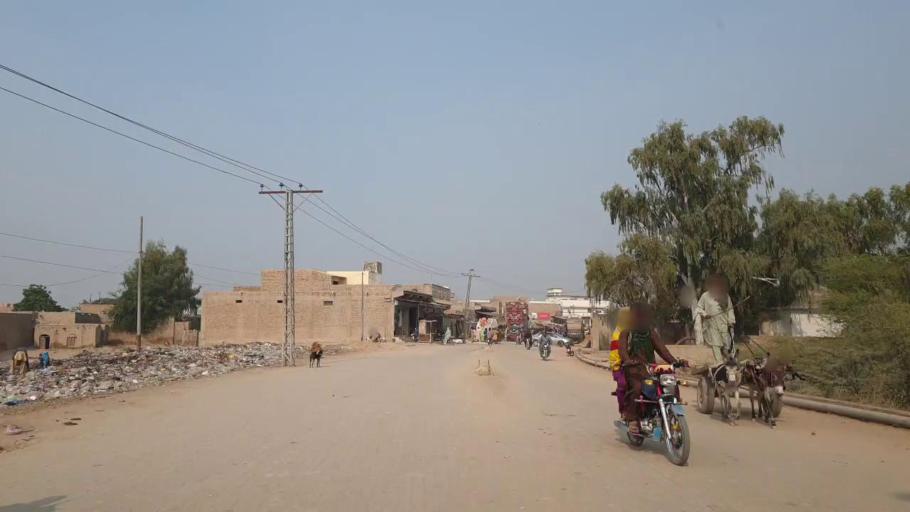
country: PK
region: Sindh
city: Bhan
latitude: 26.5537
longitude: 67.7186
